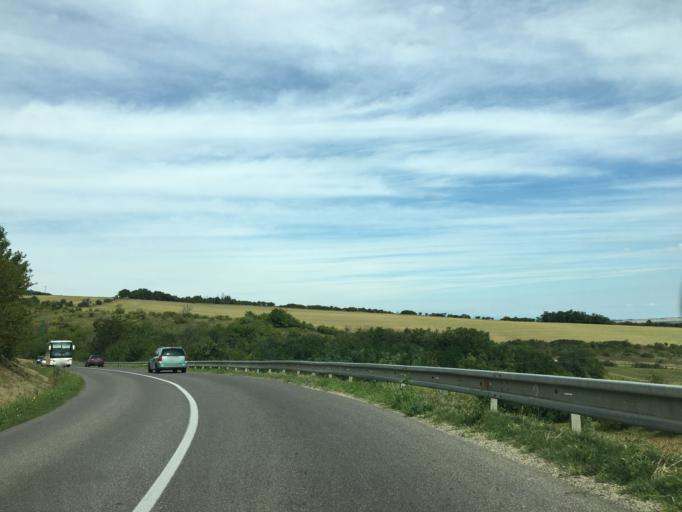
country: HU
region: Komarom-Esztergom
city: Esztergom
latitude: 47.8603
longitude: 18.7432
